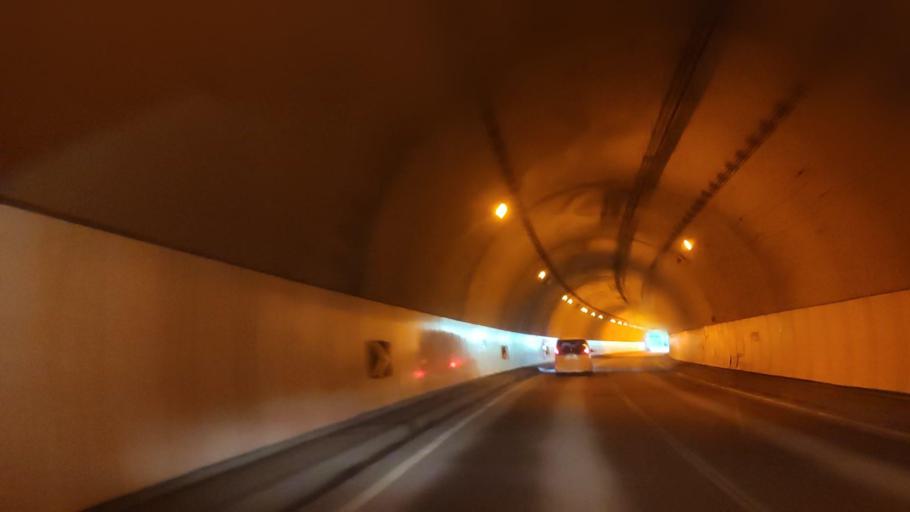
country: JP
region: Hokkaido
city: Ashibetsu
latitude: 43.3776
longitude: 142.2191
